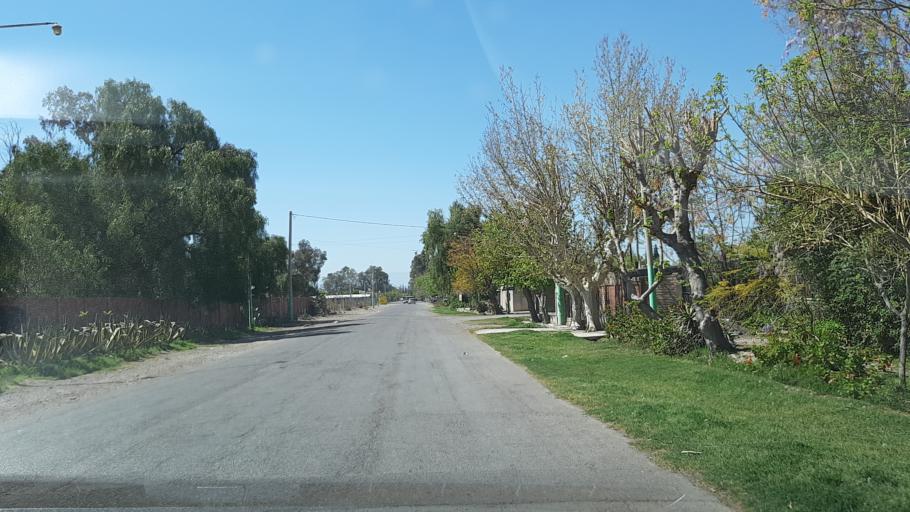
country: AR
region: San Juan
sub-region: Departamento de Rivadavia
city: Rivadavia
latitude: -31.5247
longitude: -68.6303
